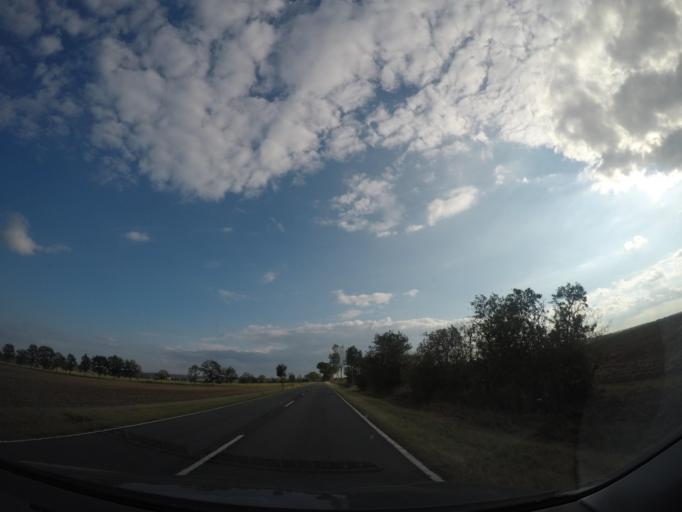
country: DE
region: Saxony-Anhalt
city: Weferlingen
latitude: 52.3841
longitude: 11.1022
